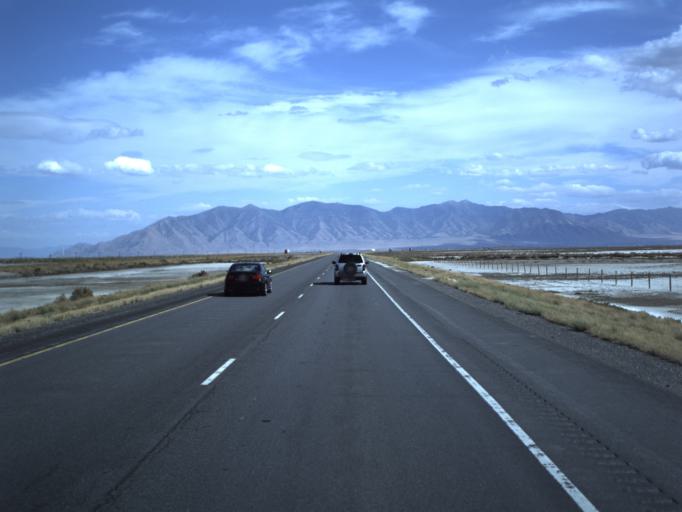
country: US
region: Utah
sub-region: Tooele County
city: Grantsville
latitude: 40.7029
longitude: -112.5023
